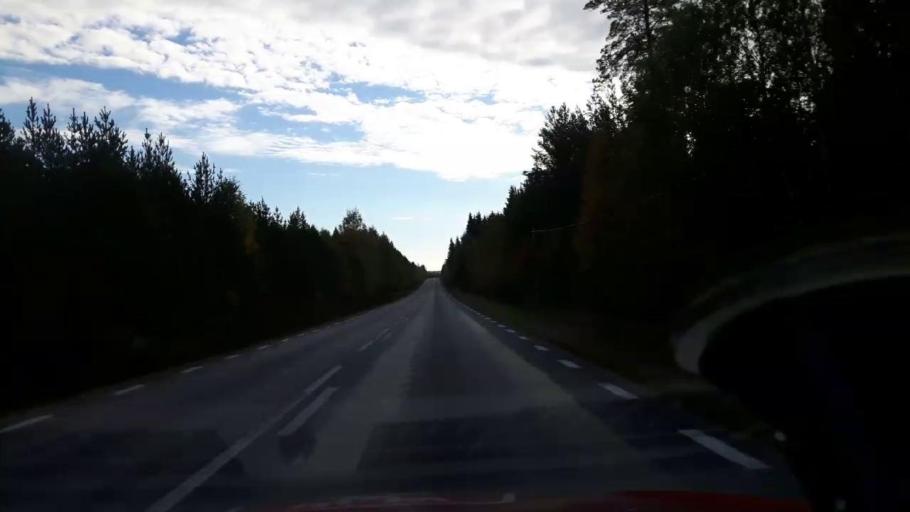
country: SE
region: Gaevleborg
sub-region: Ljusdals Kommun
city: Farila
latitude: 61.9920
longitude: 15.2611
